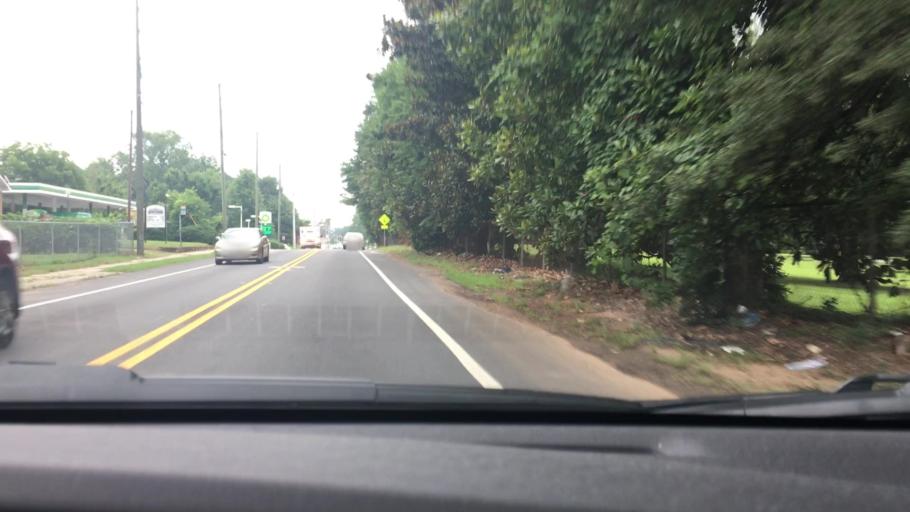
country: US
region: Georgia
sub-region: Fulton County
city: Atlanta
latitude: 33.7489
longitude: -84.4433
